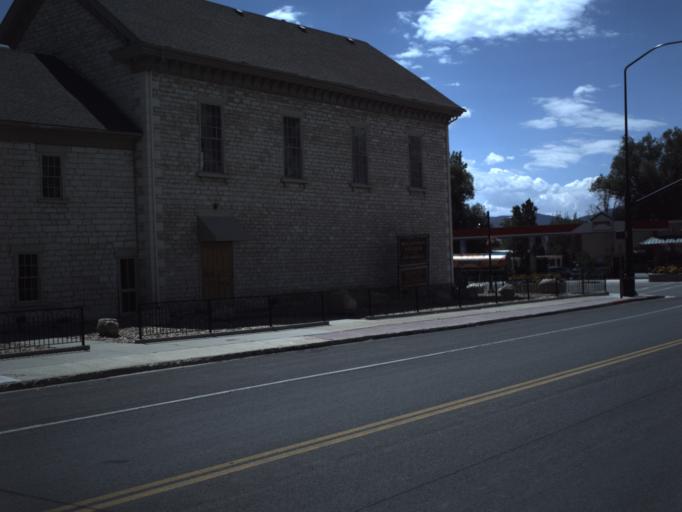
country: US
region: Utah
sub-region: Sanpete County
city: Ephraim
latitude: 39.3617
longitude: -111.5864
